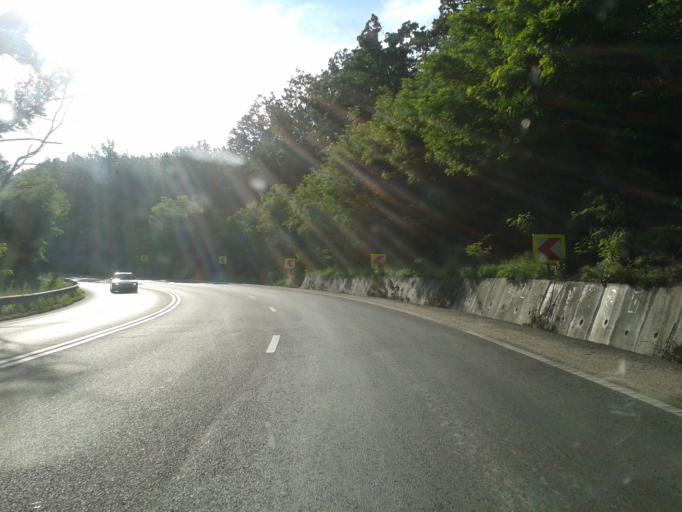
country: RO
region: Hunedoara
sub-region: Comuna Santamaria-Orlea
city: Santamaria-Orlea
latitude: 45.6152
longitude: 22.9839
